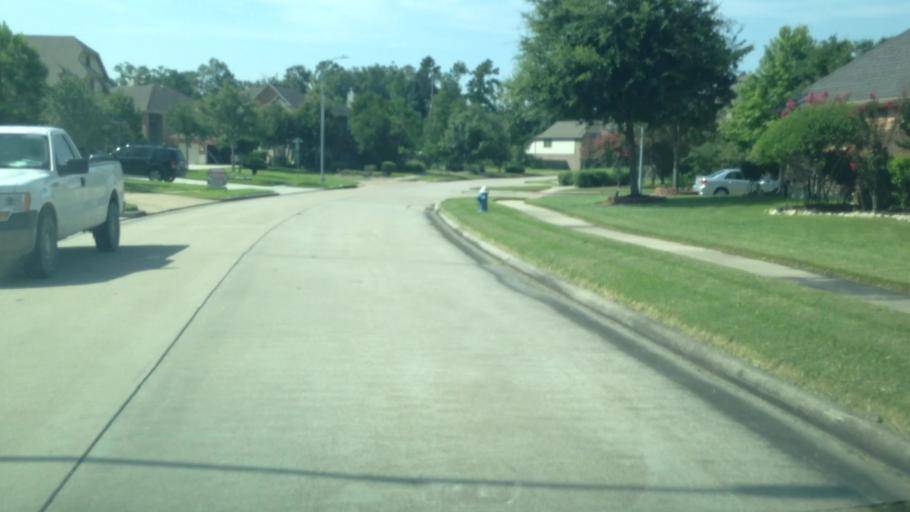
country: US
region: Texas
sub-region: Harris County
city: Sheldon
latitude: 29.9203
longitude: -95.1710
